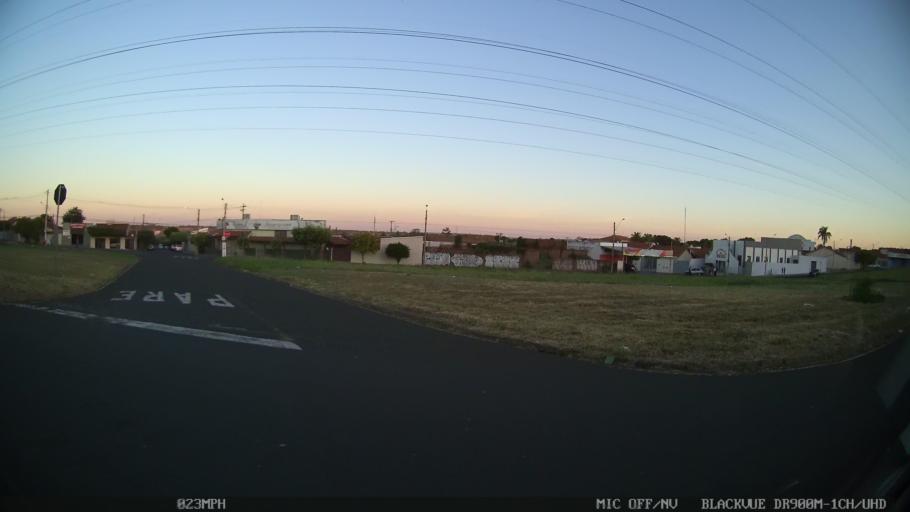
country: BR
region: Sao Paulo
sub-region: Sao Jose Do Rio Preto
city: Sao Jose do Rio Preto
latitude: -20.8435
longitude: -49.3783
